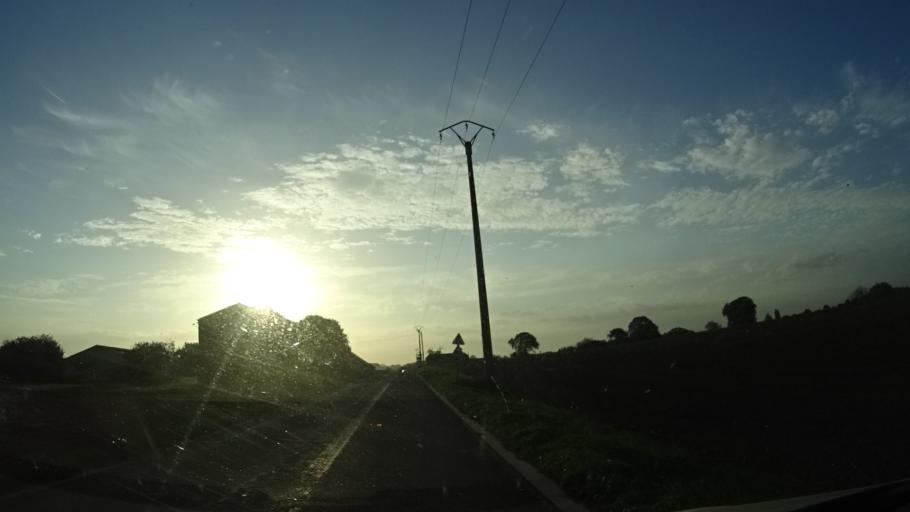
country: BE
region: Wallonia
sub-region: Province du Hainaut
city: Beaumont
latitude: 50.2649
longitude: 4.2254
